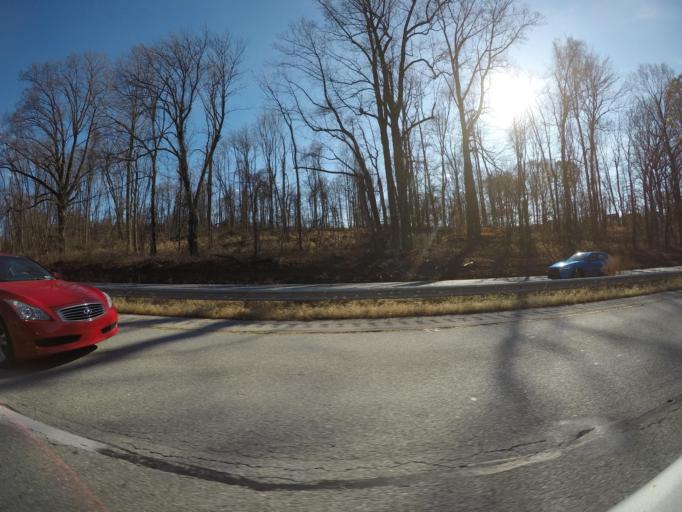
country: US
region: Pennsylvania
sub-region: Chester County
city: Coatesville
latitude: 40.0008
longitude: -75.8117
